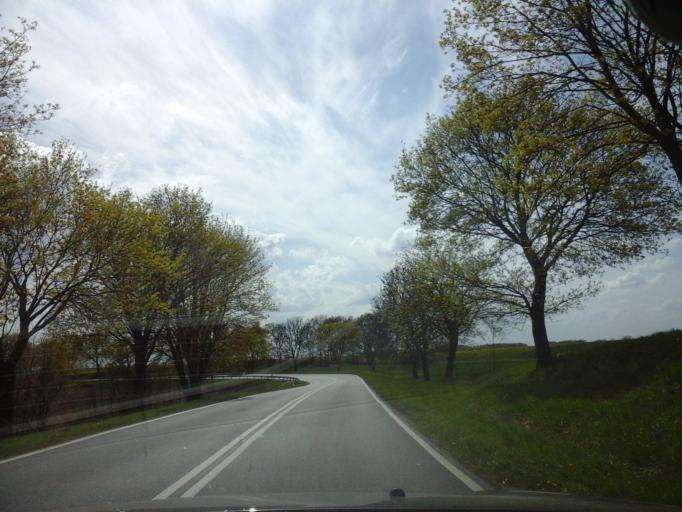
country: PL
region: West Pomeranian Voivodeship
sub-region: Powiat choszczenski
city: Choszczno
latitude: 53.1495
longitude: 15.3800
